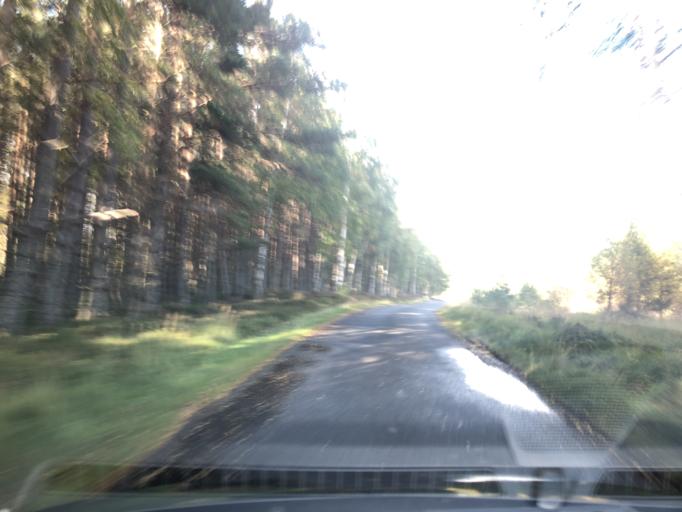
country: GB
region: Scotland
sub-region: Highland
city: Aviemore
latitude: 57.0705
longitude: -3.9022
